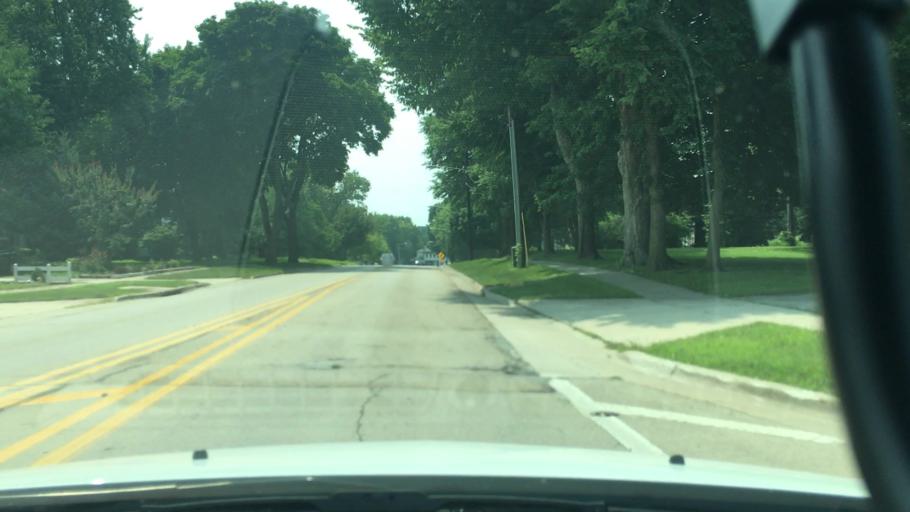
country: US
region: Illinois
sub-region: Ogle County
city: Rochelle
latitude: 41.9320
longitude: -89.0684
